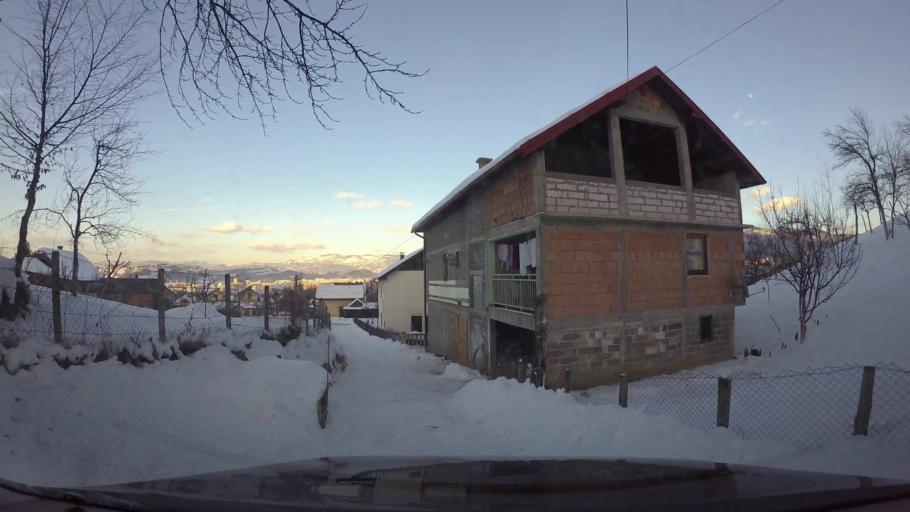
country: BA
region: Federation of Bosnia and Herzegovina
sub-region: Kanton Sarajevo
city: Sarajevo
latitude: 43.8074
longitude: 18.3557
